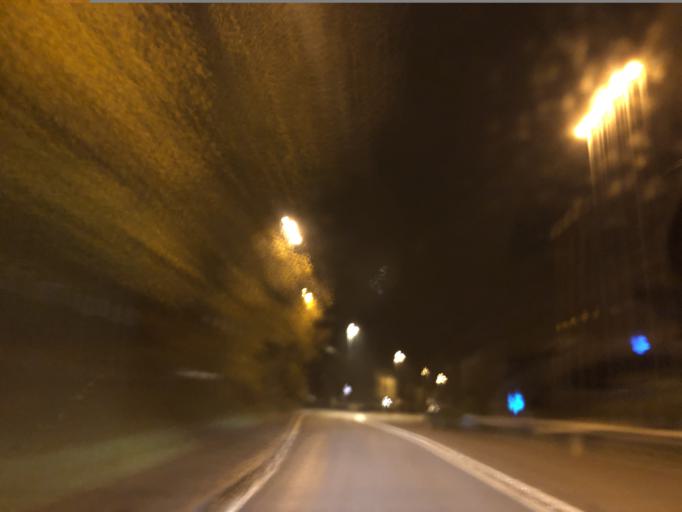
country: GB
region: England
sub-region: Borough of Oldham
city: Delph
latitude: 53.5832
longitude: -2.0491
